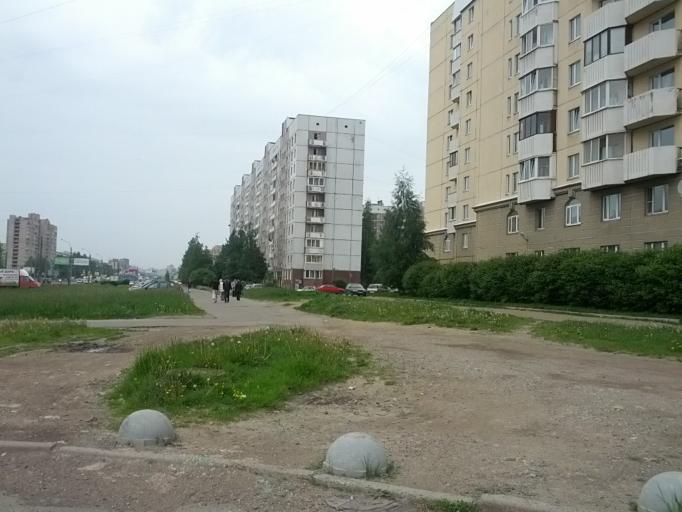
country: RU
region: Leningrad
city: Rybatskoye
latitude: 59.8974
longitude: 30.4922
